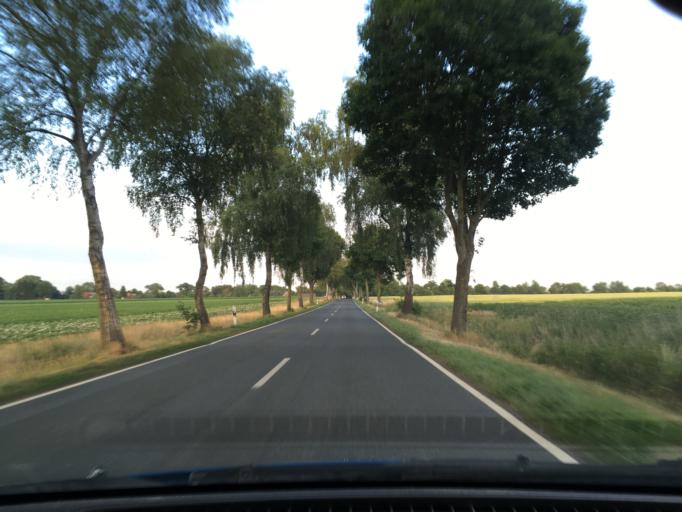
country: DE
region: Lower Saxony
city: Scharnhorst
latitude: 52.7205
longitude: 10.3053
